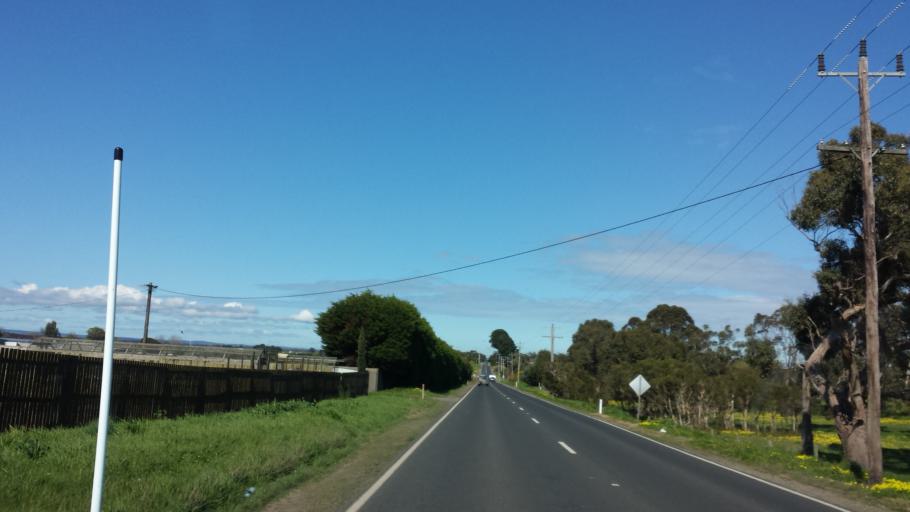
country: AU
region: Victoria
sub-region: Casey
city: Junction Village
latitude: -38.1435
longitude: 145.3222
